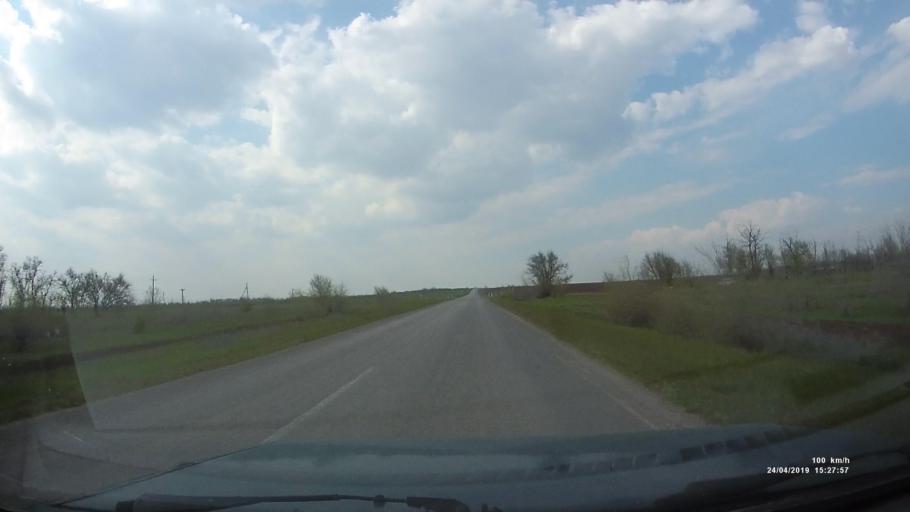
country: RU
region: Rostov
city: Remontnoye
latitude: 46.5722
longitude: 43.0219
